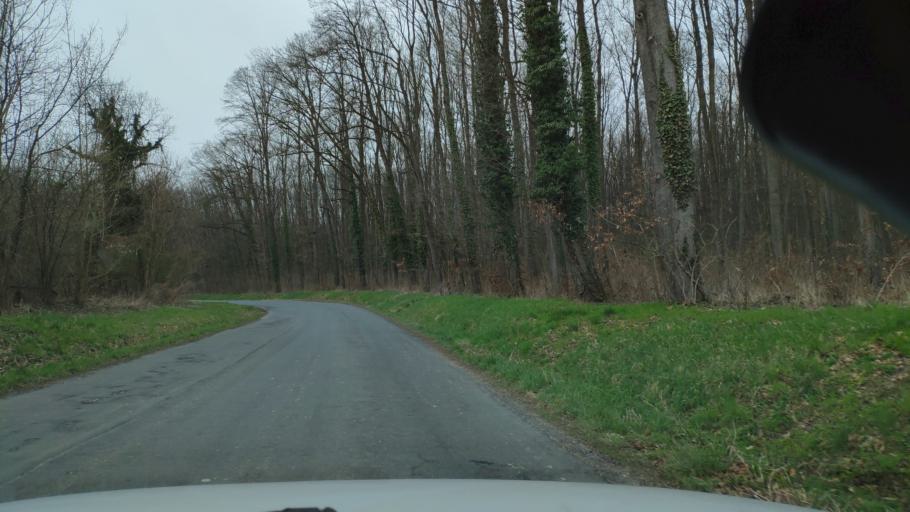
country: HU
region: Zala
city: Sarmellek
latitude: 46.6771
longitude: 17.1056
